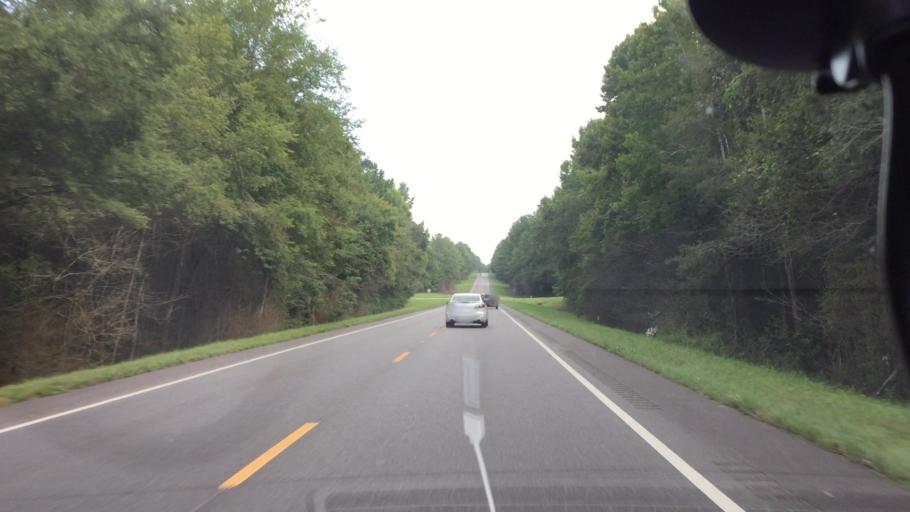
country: US
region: Alabama
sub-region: Pike County
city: Brundidge
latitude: 31.5860
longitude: -85.9383
